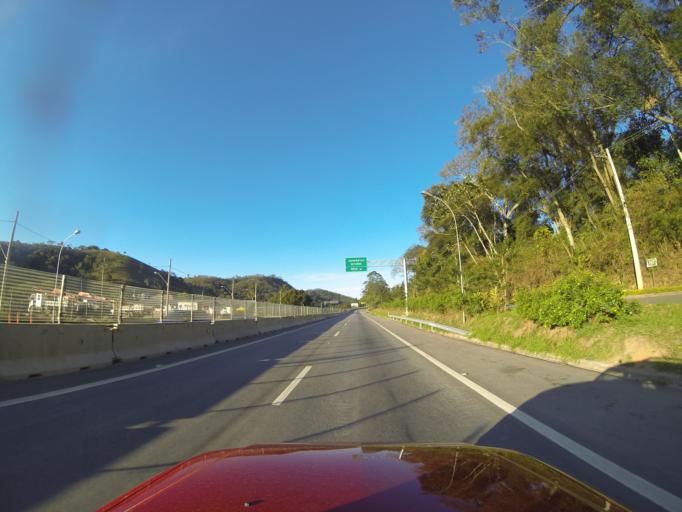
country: BR
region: Sao Paulo
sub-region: Santa Branca
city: Santa Branca
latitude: -23.3195
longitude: -45.7345
